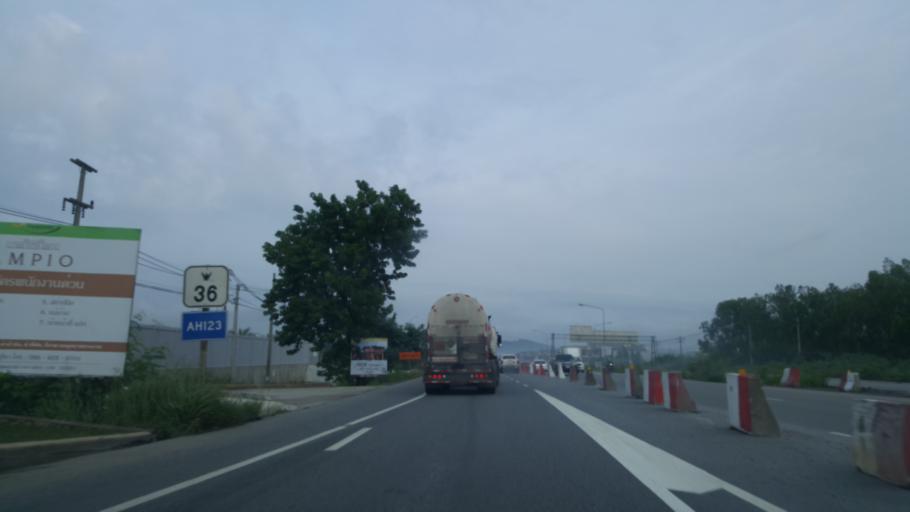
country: TH
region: Chon Buri
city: Phatthaya
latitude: 12.9140
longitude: 101.0238
